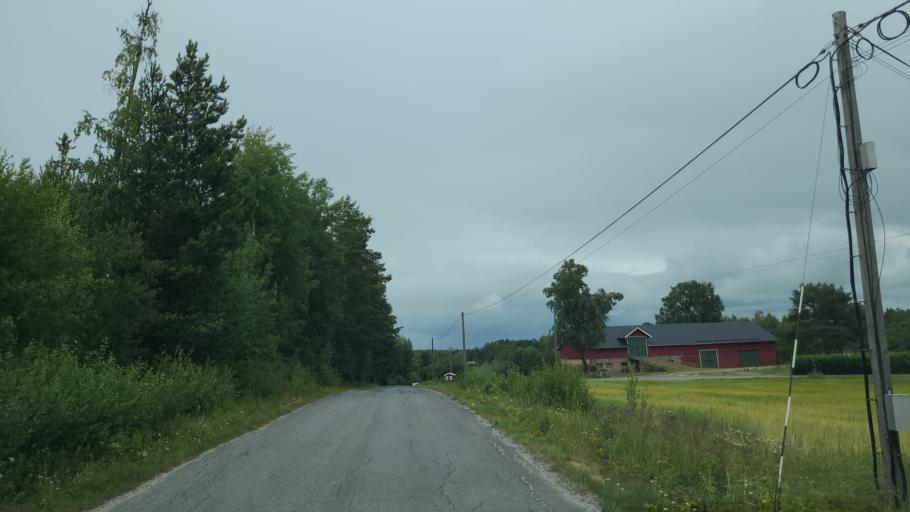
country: FI
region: Varsinais-Suomi
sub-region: Aboland-Turunmaa
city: Dragsfjaerd
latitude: 60.0945
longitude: 22.4349
